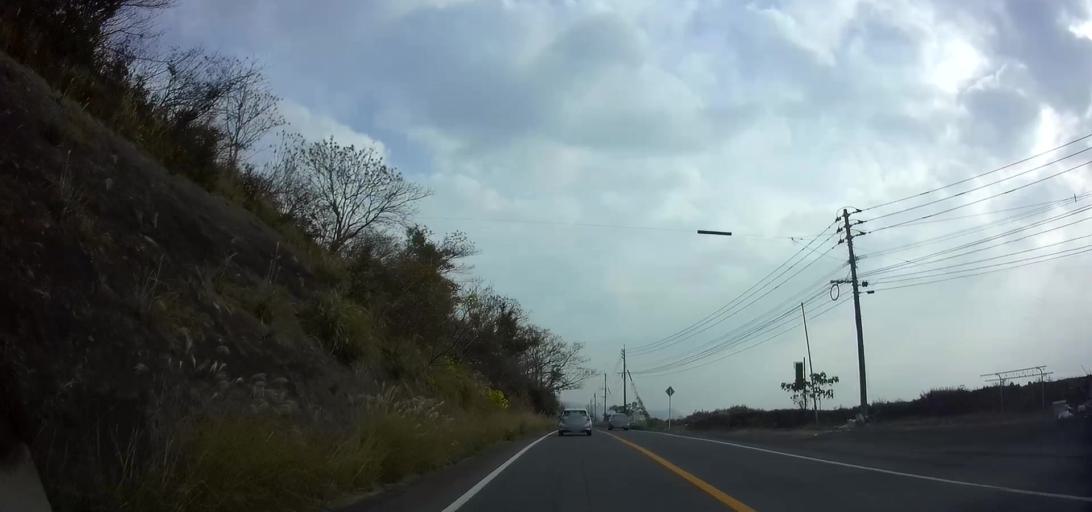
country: JP
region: Nagasaki
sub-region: Isahaya-shi
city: Isahaya
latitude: 32.7910
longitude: 130.0581
